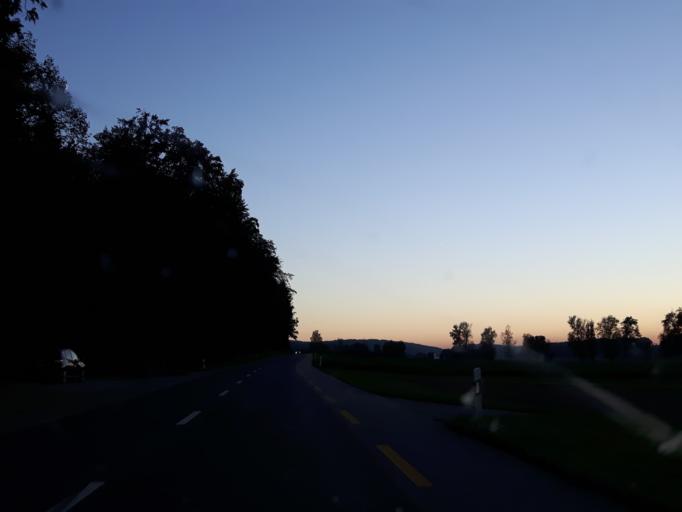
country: CH
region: Bern
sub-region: Oberaargau
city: Lotzwil
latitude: 47.1950
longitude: 7.7679
